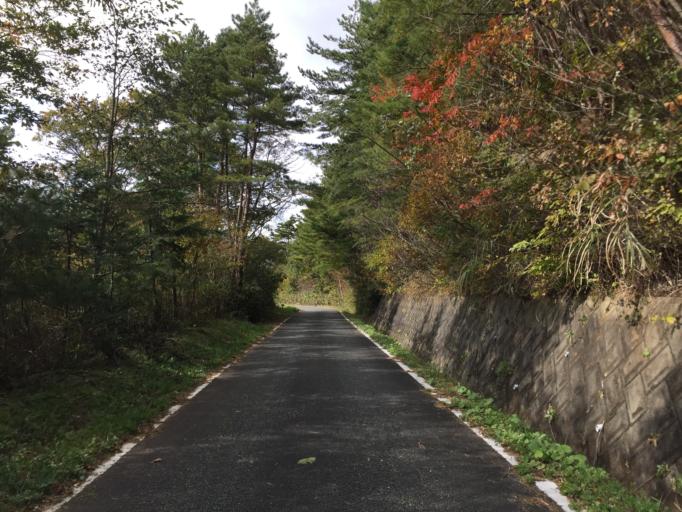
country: JP
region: Fukushima
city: Nihommatsu
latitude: 37.6788
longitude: 140.3719
